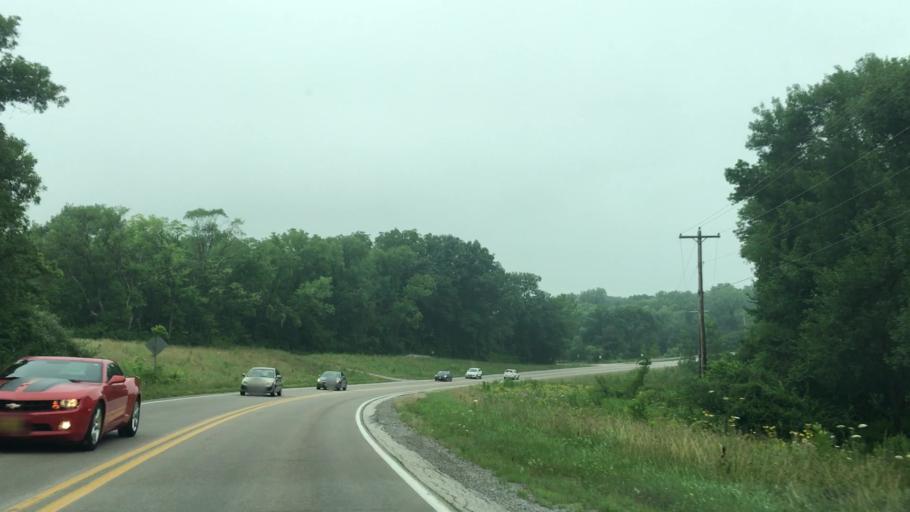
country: US
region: Iowa
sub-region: Johnson County
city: Iowa City
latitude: 41.6910
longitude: -91.5465
